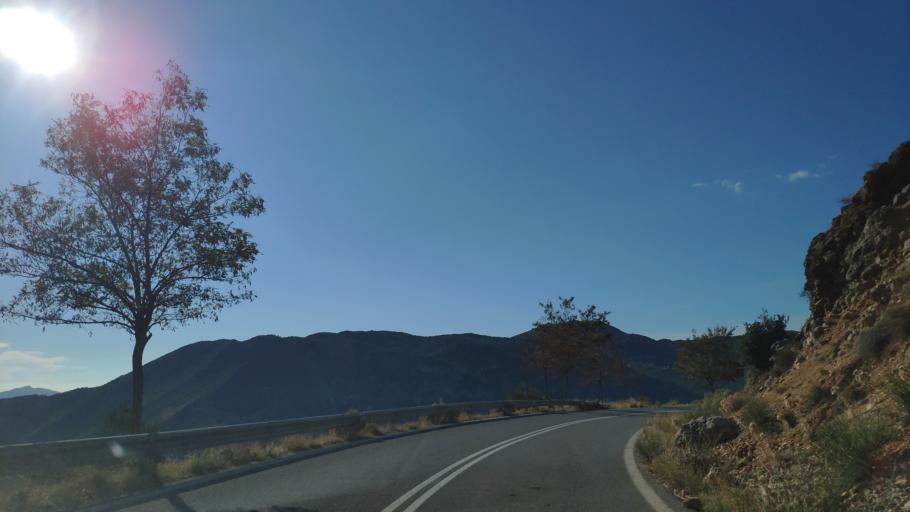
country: GR
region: Peloponnese
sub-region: Nomos Arkadias
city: Dimitsana
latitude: 37.5799
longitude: 22.0586
